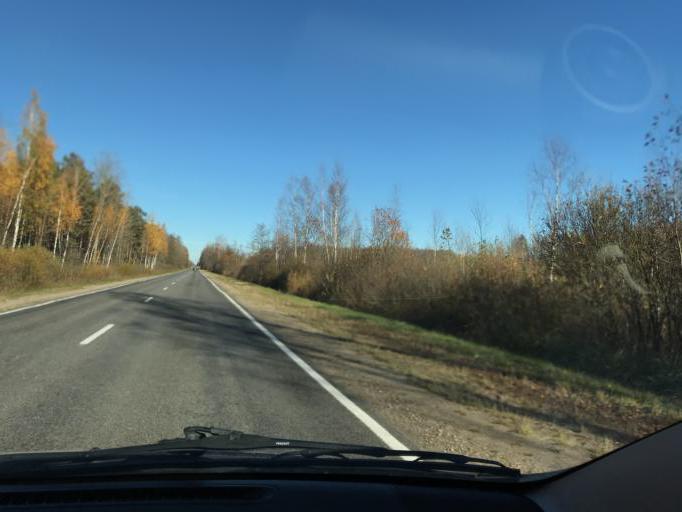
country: BY
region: Vitebsk
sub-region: Ushatski Rayon
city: Ushachy
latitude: 55.0721
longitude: 28.7542
